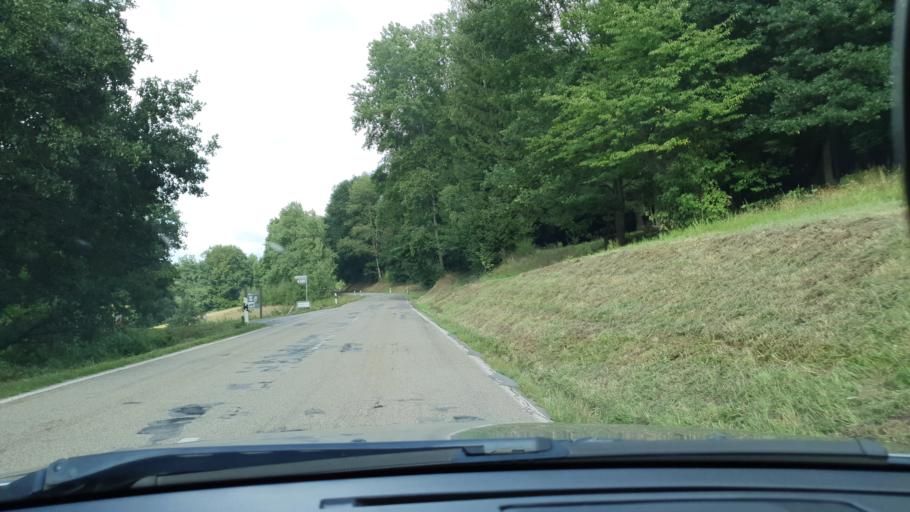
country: DE
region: Rheinland-Pfalz
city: Massweiler
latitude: 49.2637
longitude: 7.5461
